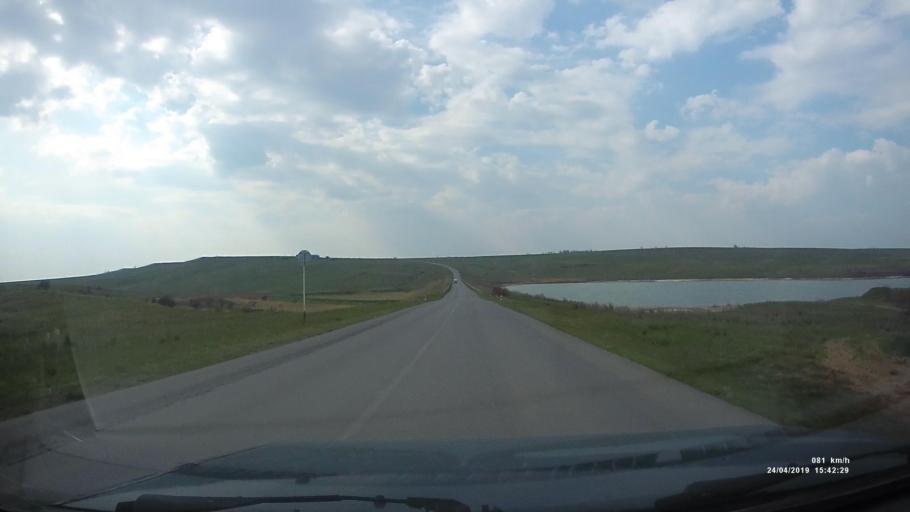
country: RU
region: Kalmykiya
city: Yashalta
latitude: 46.5764
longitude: 42.7875
